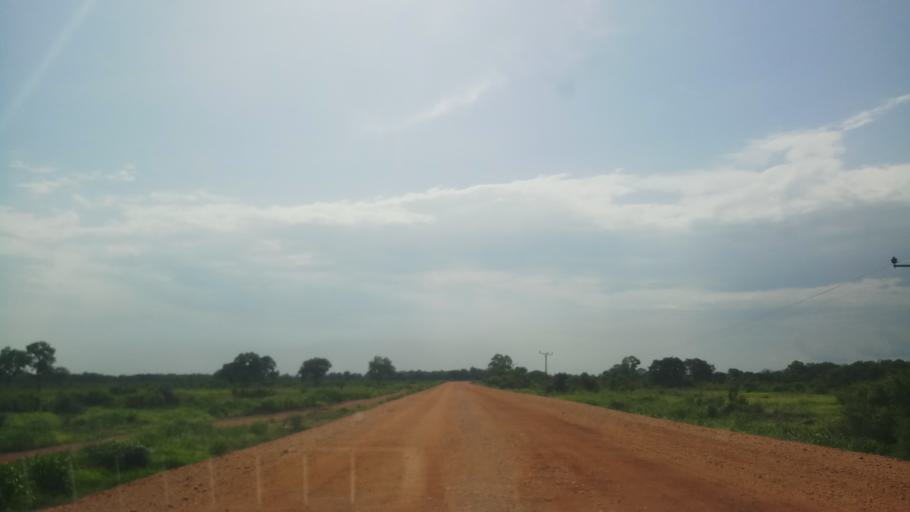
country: ET
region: Gambela
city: Gambela
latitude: 8.1330
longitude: 34.3821
